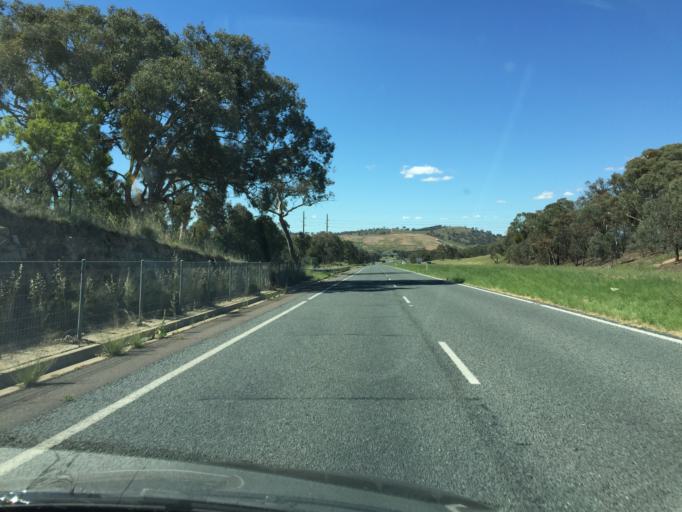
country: AU
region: Australian Capital Territory
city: Macarthur
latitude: -35.4145
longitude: 149.1446
